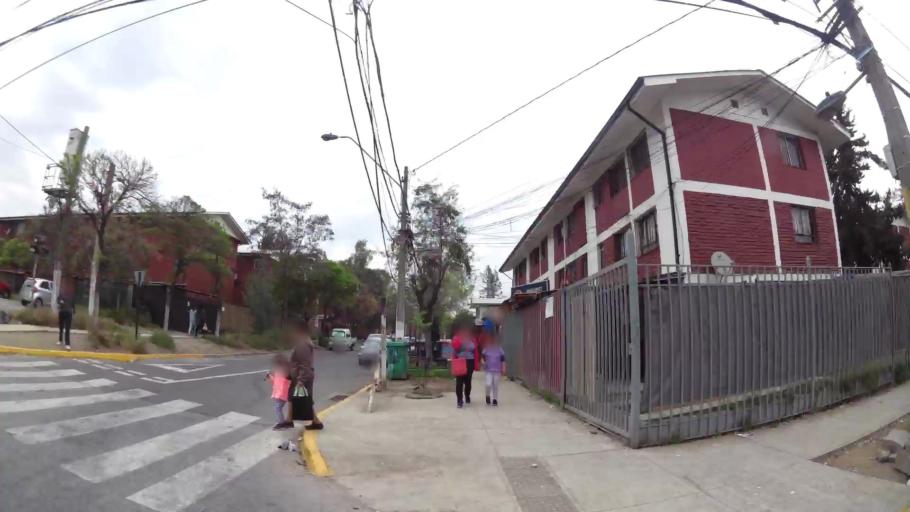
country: CL
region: Santiago Metropolitan
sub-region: Provincia de Santiago
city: Villa Presidente Frei, Nunoa, Santiago, Chile
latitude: -33.4998
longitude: -70.5899
